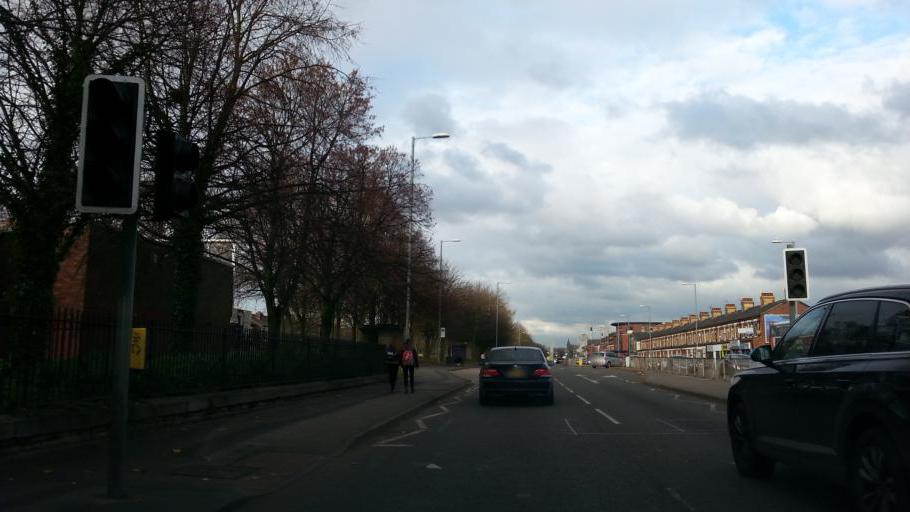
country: GB
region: England
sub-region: Manchester
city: Hulme
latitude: 53.4513
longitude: -2.2451
